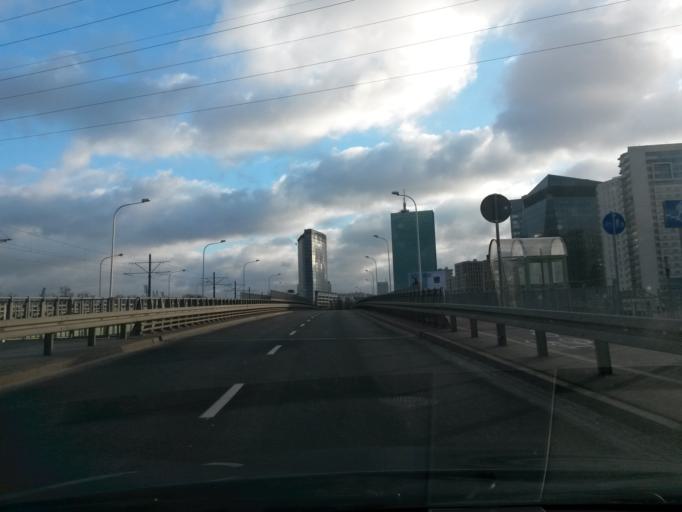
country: PL
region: Masovian Voivodeship
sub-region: Warszawa
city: Zoliborz
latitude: 52.2599
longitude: 20.9947
